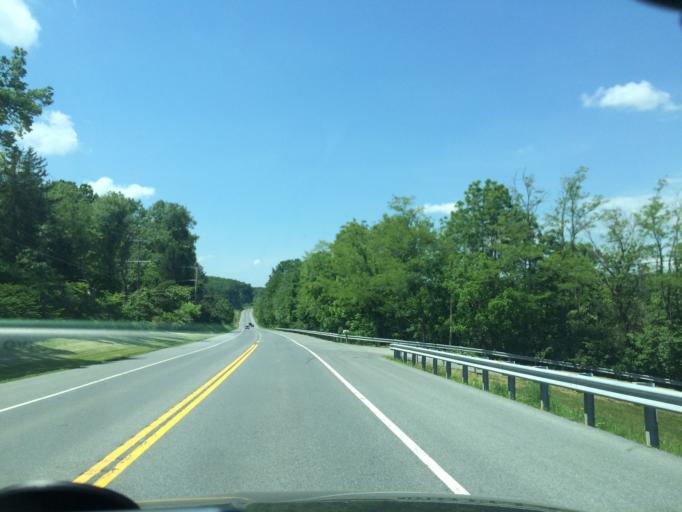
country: US
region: Maryland
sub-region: Carroll County
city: Eldersburg
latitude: 39.4755
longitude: -76.9164
